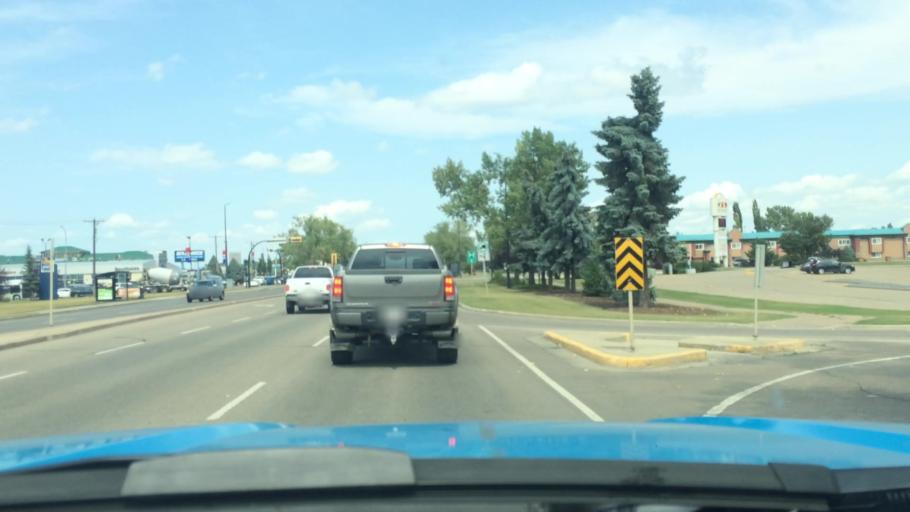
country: CA
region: Alberta
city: Red Deer
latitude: 52.2436
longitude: -113.8139
